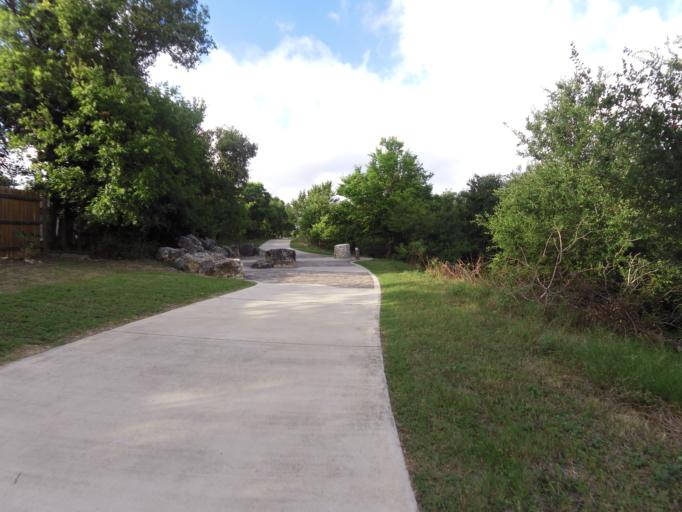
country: US
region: Texas
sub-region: Bexar County
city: Leon Valley
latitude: 29.4969
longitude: -98.6369
